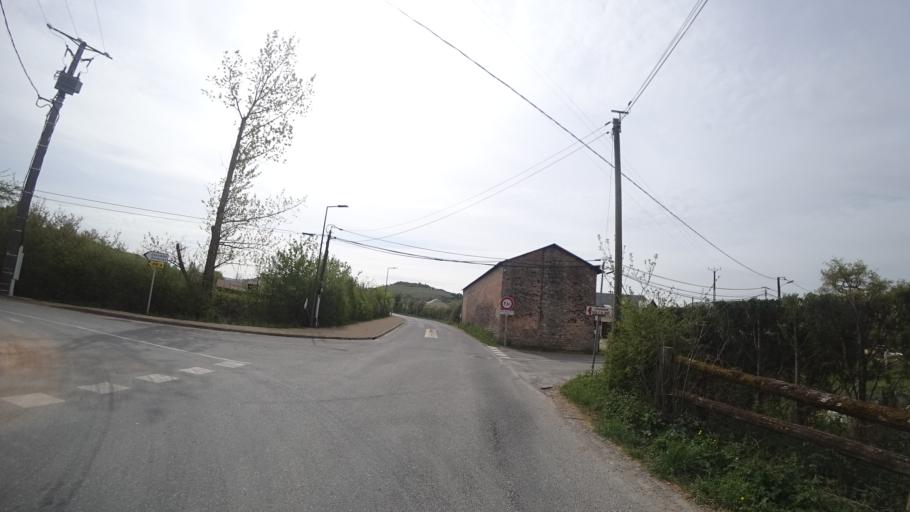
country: FR
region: Midi-Pyrenees
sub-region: Departement de l'Aveyron
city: Sebazac-Concoures
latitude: 44.3790
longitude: 2.6038
